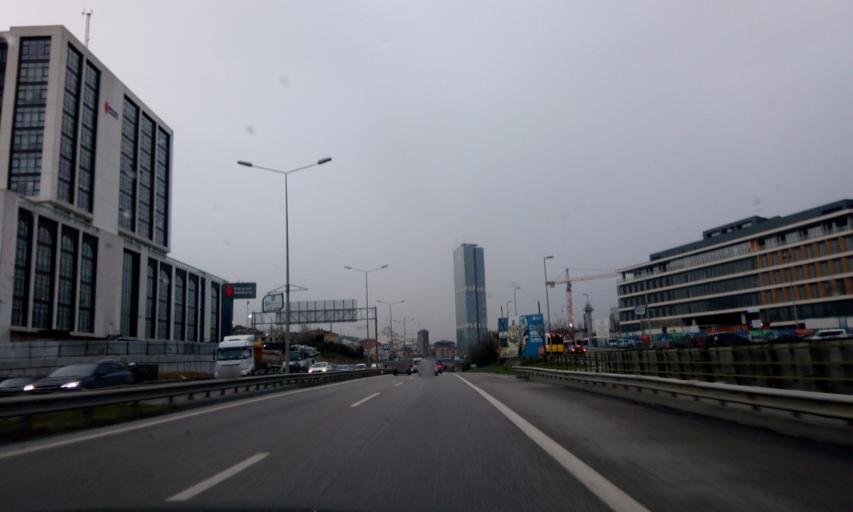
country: TR
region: Istanbul
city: Umraniye
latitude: 41.0301
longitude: 29.1009
